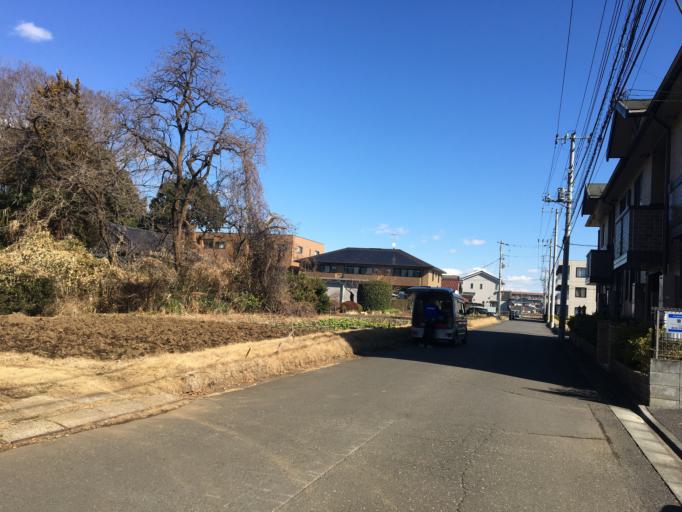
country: JP
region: Saitama
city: Kamifukuoka
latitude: 35.8832
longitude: 139.4985
